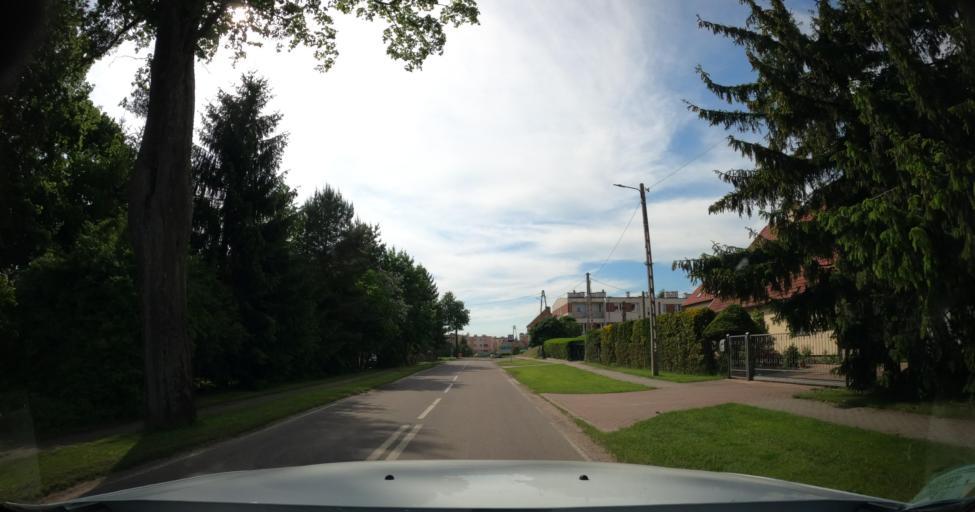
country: PL
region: Warmian-Masurian Voivodeship
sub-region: Powiat ostrodzki
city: Milakowo
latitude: 54.0079
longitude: 20.0805
